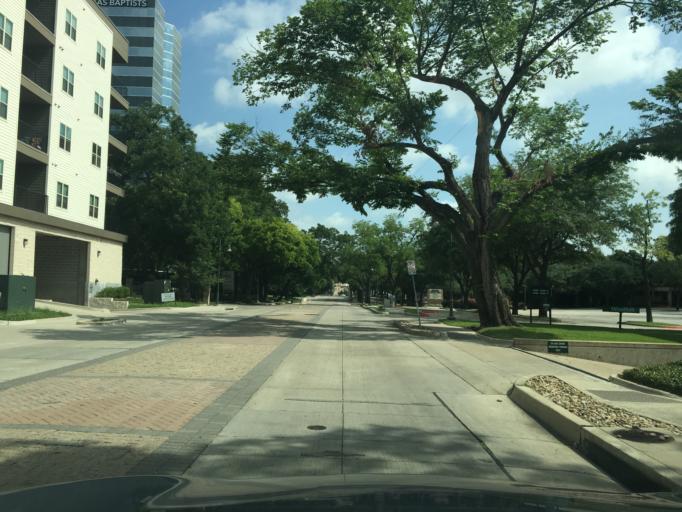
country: US
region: Texas
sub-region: Dallas County
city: University Park
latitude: 32.8839
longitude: -96.7624
